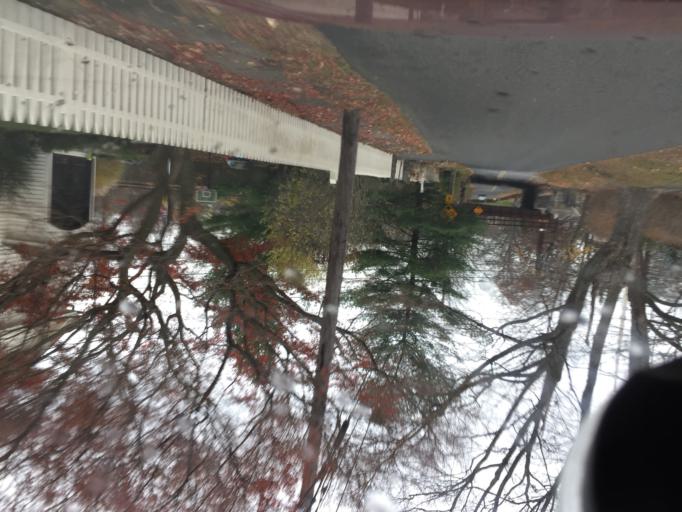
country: US
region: Connecticut
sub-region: Fairfield County
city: Southport
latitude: 41.1333
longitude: -73.2925
